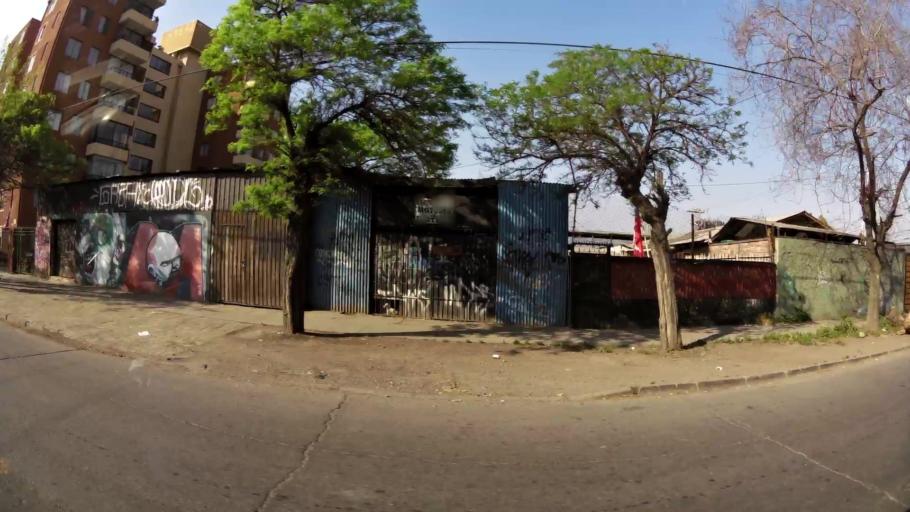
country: CL
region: Santiago Metropolitan
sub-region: Provincia de Santiago
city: Lo Prado
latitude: -33.3821
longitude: -70.6823
